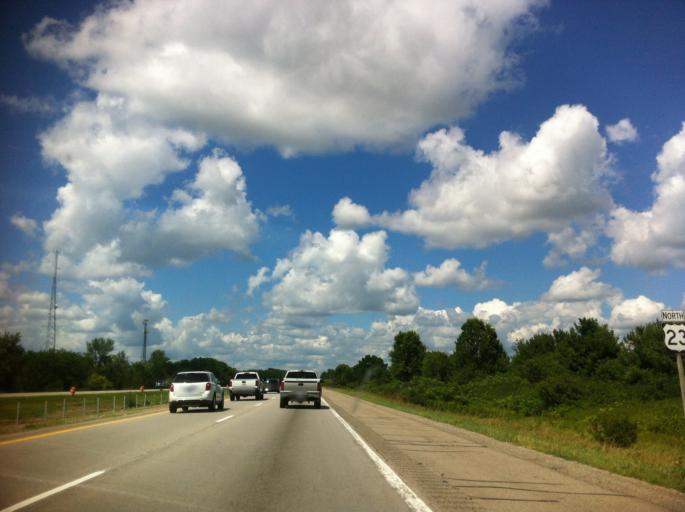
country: US
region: Michigan
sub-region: Washtenaw County
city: Milan
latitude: 42.1653
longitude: -83.6842
